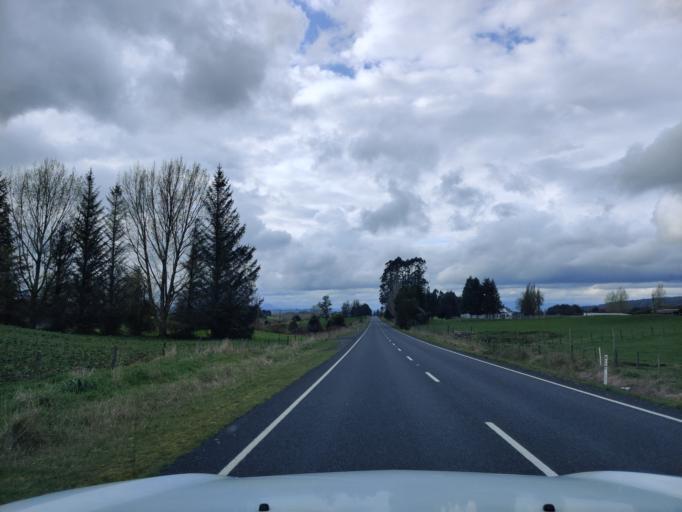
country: NZ
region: Waikato
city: Turangi
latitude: -39.0489
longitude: 175.3836
